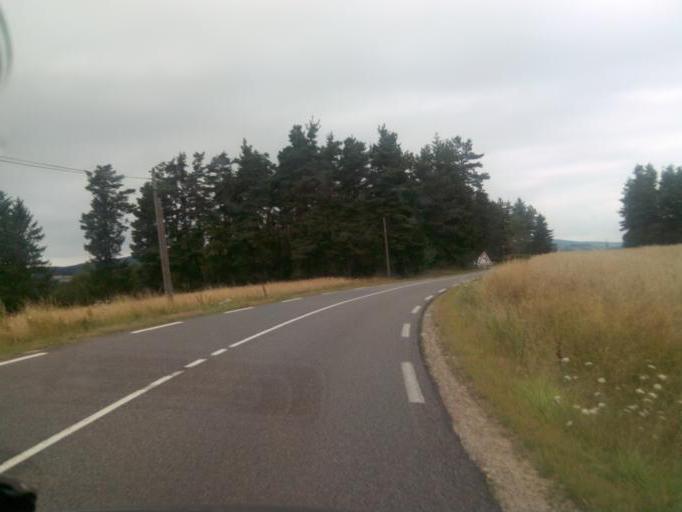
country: FR
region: Rhone-Alpes
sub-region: Departement de la Loire
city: Usson-en-Forez
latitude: 45.3565
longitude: 3.9011
